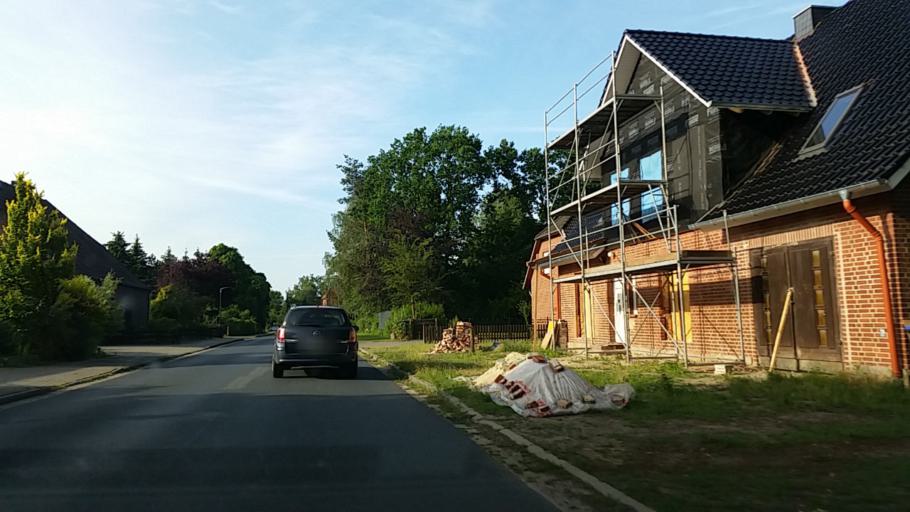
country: DE
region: Lower Saxony
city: Wieren
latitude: 52.9320
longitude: 10.6421
